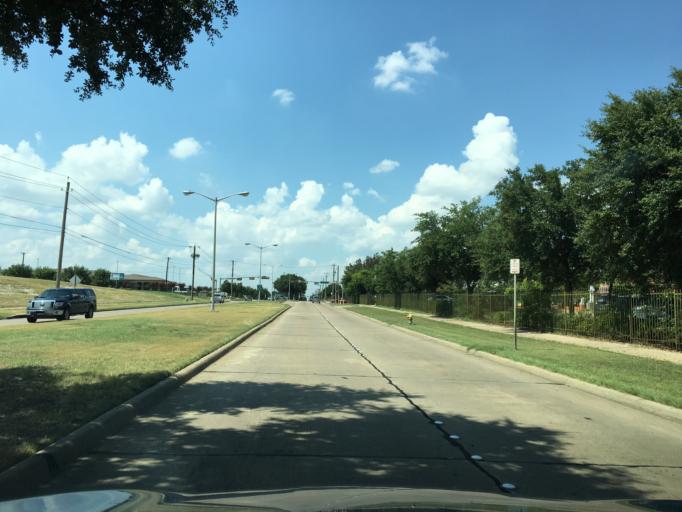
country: US
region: Texas
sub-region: Dallas County
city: Garland
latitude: 32.9488
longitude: -96.6502
